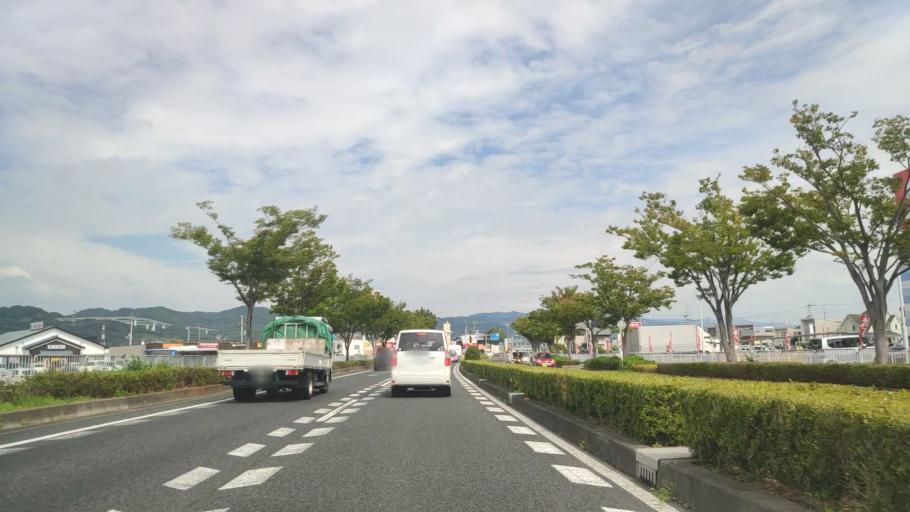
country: JP
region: Wakayama
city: Iwade
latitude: 34.2614
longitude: 135.2655
